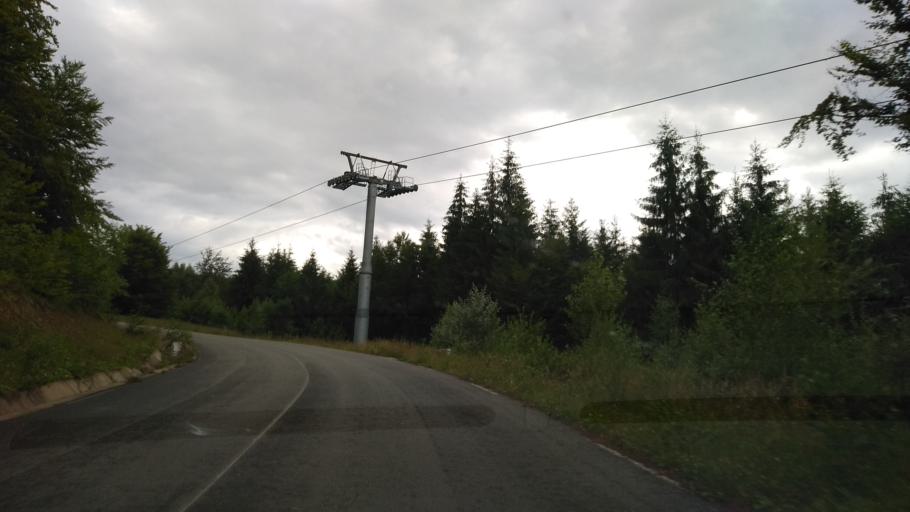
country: RO
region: Hunedoara
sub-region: Municipiul  Vulcan
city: Jiu-Paroseni
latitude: 45.3465
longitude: 23.2906
